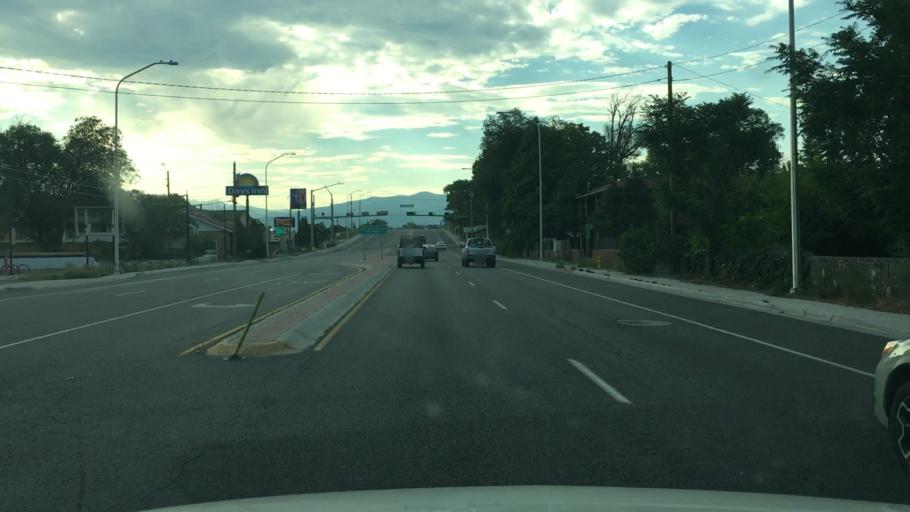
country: US
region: New Mexico
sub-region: Rio Arriba County
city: Espanola
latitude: 35.9874
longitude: -106.0600
